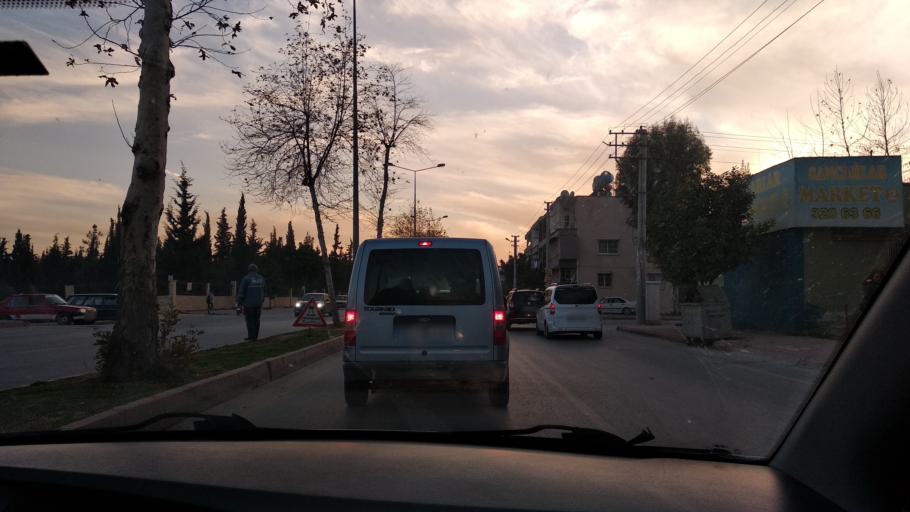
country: TR
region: Mersin
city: Mercin
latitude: 36.8234
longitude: 34.6015
